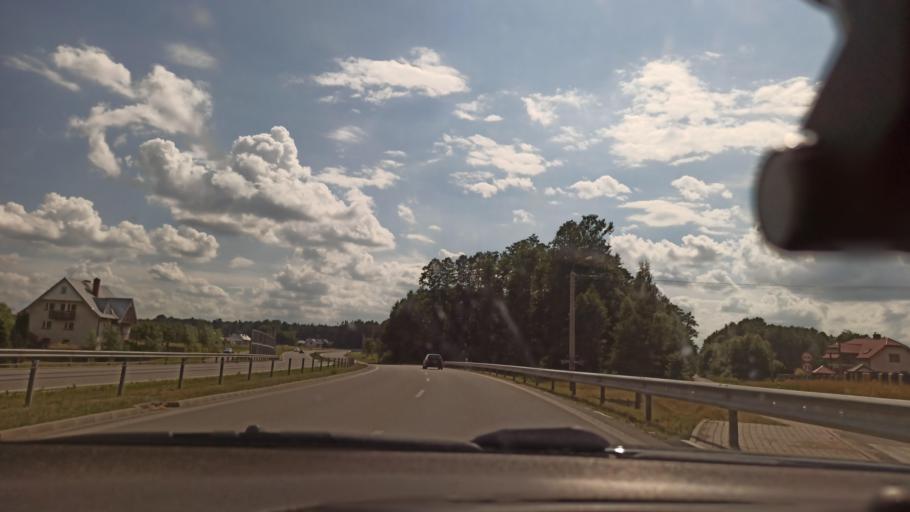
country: PL
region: Podlasie
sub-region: Powiat bialostocki
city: Turosn Koscielna
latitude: 53.0634
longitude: 23.0660
